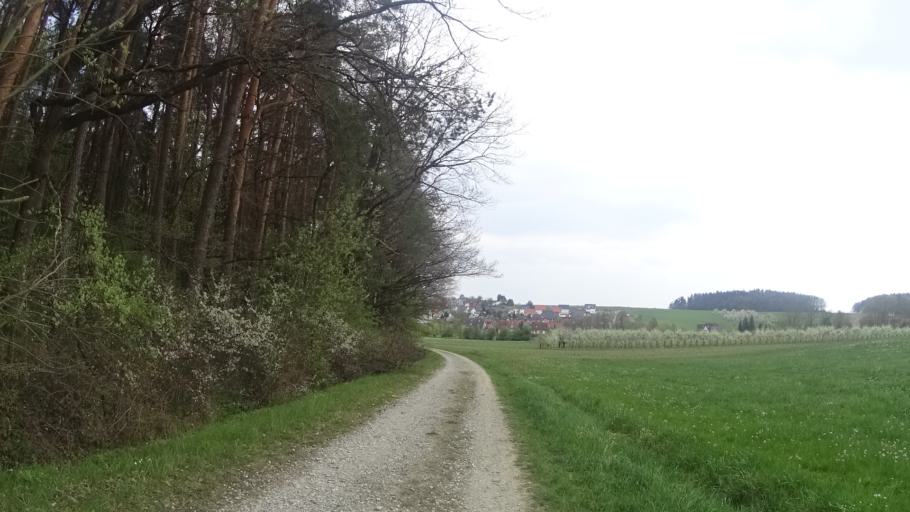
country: DE
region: Bavaria
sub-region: Upper Franconia
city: Igensdorf
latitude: 49.6201
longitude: 11.2179
